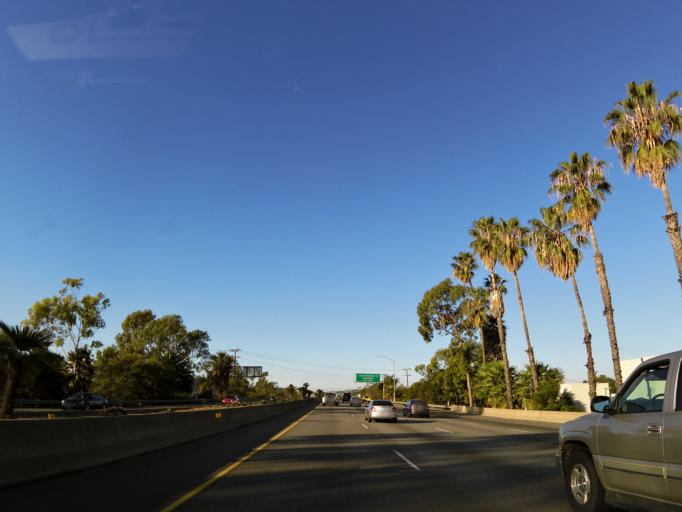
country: US
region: California
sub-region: Santa Barbara County
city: Santa Barbara
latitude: 34.4202
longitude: -119.6799
